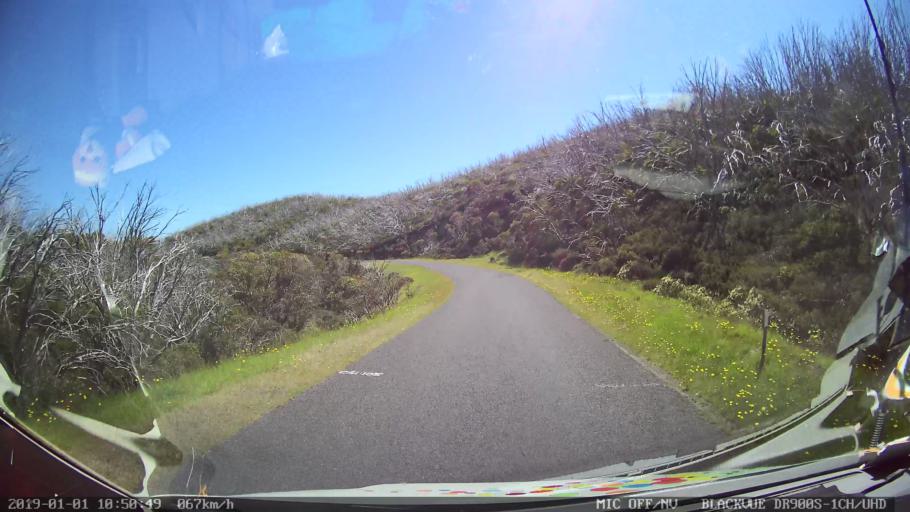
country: AU
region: New South Wales
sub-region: Snowy River
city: Jindabyne
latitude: -36.0247
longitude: 148.3719
